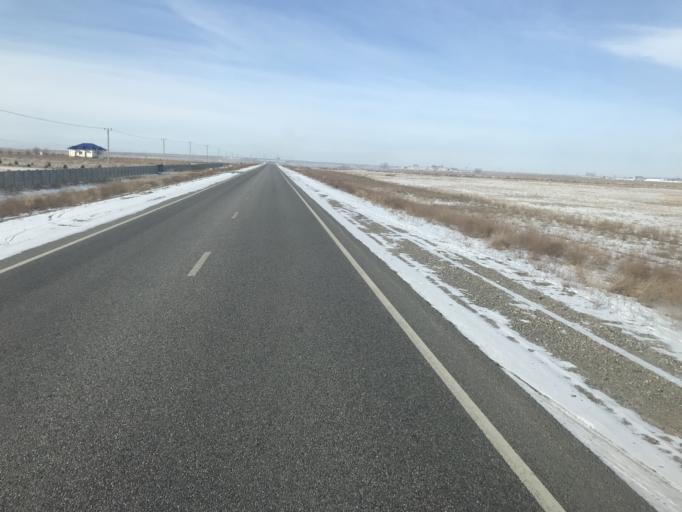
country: KZ
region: Zhambyl
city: Sarykemer
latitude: 43.0507
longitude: 71.4688
